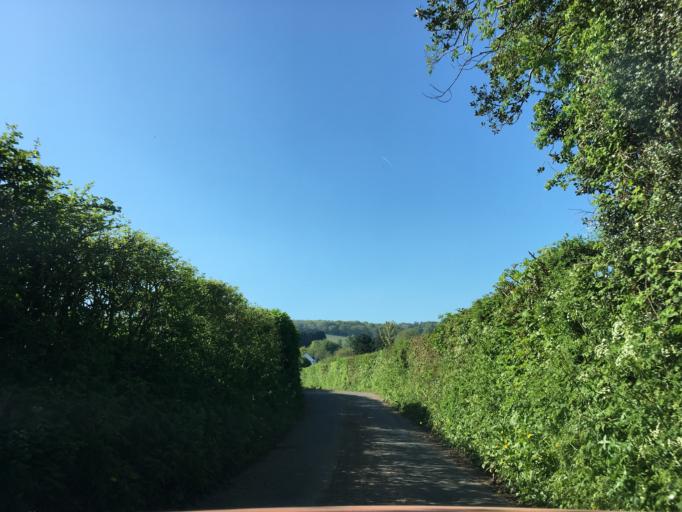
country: GB
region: Wales
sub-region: Newport
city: Llanvaches
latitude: 51.6247
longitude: -2.7973
